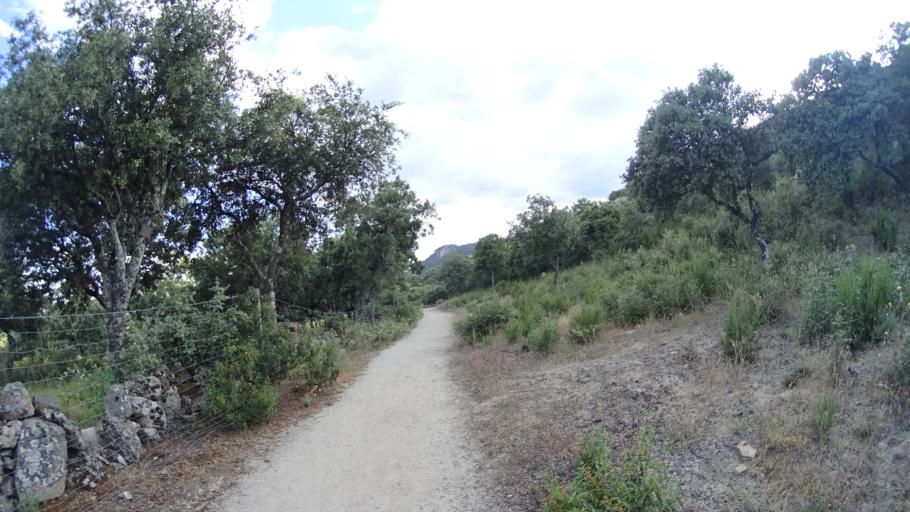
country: ES
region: Madrid
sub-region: Provincia de Madrid
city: Hoyo de Manzanares
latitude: 40.6340
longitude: -3.9089
